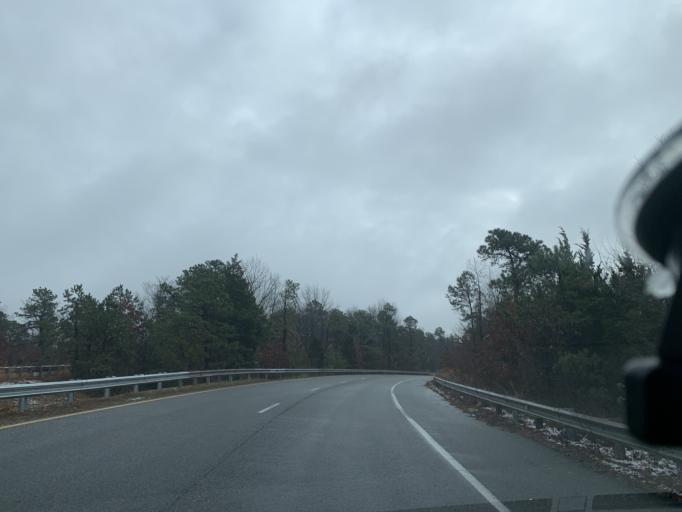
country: US
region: New Jersey
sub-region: Atlantic County
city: Pomona
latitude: 39.4496
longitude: -74.6266
